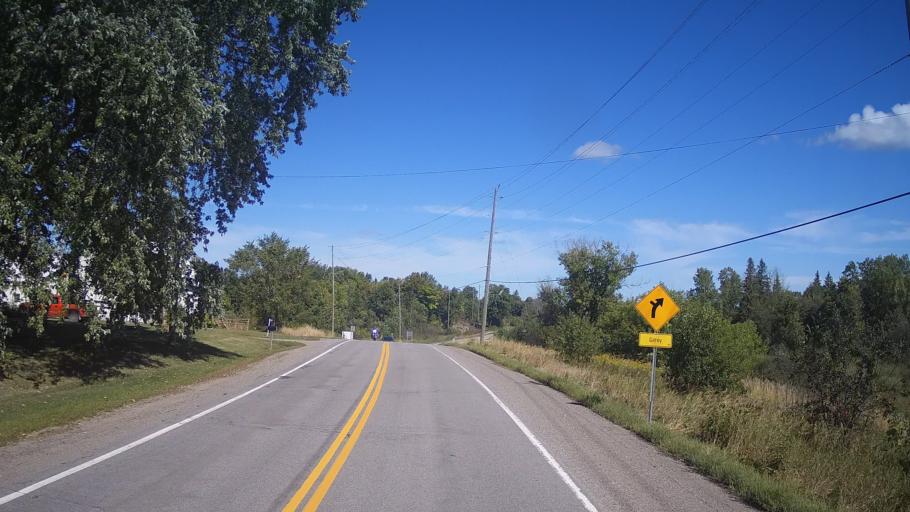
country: CA
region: Ontario
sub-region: Lanark County
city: Smiths Falls
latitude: 44.9640
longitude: -75.8242
